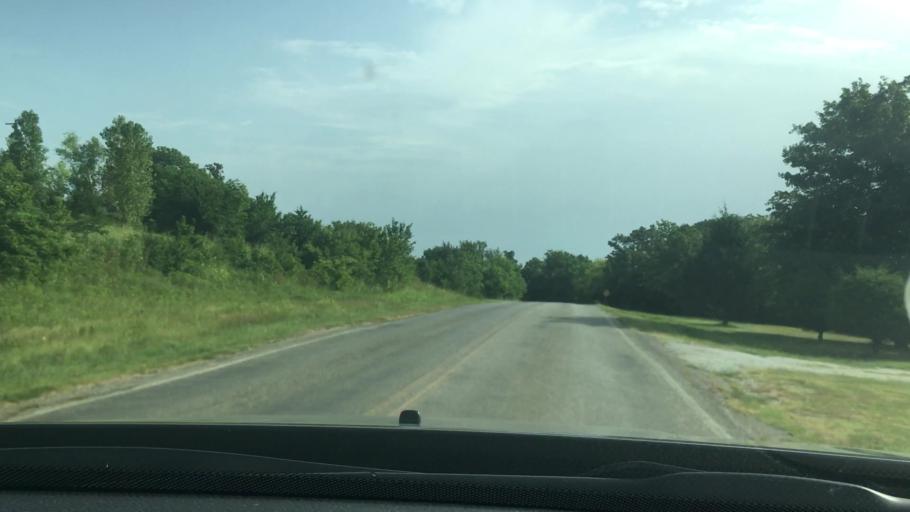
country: US
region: Oklahoma
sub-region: Pontotoc County
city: Byng
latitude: 34.8692
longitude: -96.5975
